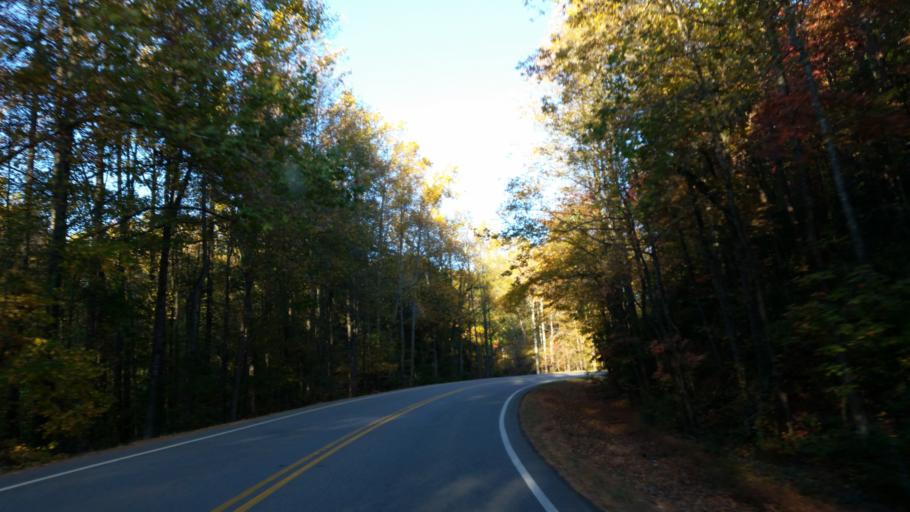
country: US
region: Georgia
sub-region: Dawson County
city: Dawsonville
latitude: 34.5545
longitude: -84.2550
